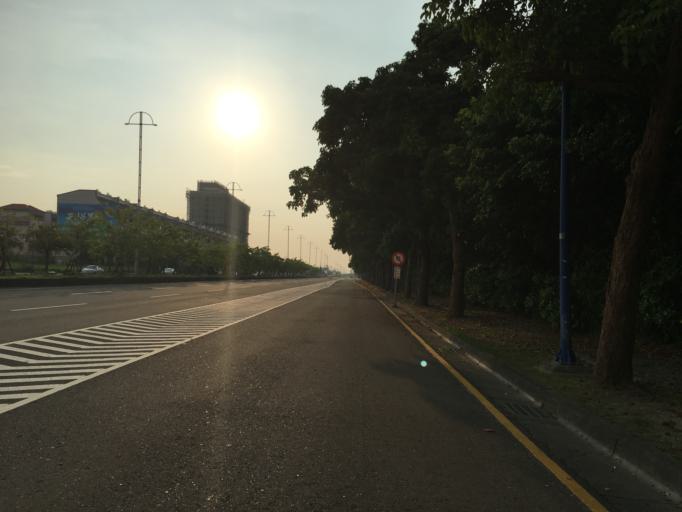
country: TW
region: Taiwan
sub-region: Chiayi
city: Taibao
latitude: 23.4689
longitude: 120.2988
